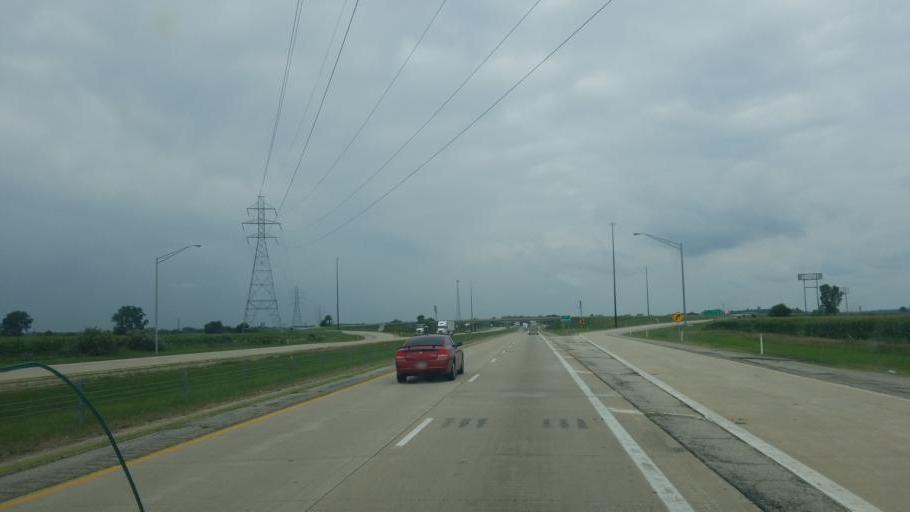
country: US
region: Indiana
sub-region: Grant County
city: Upland
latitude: 40.4191
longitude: -85.5492
